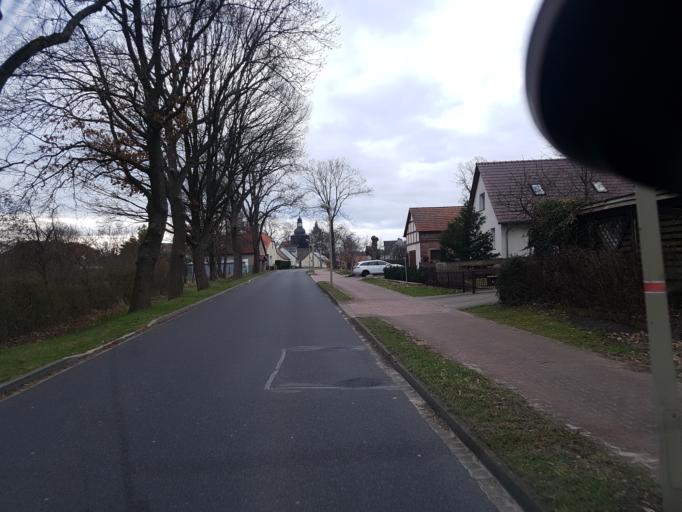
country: DE
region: Brandenburg
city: Gross Lindow
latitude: 52.1453
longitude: 14.5291
